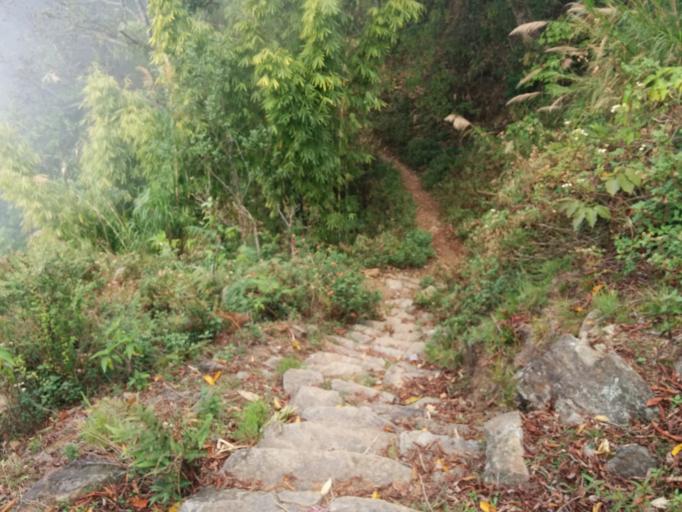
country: NP
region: Western Region
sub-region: Gandaki Zone
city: Pokhara
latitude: 28.2356
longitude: 83.9489
